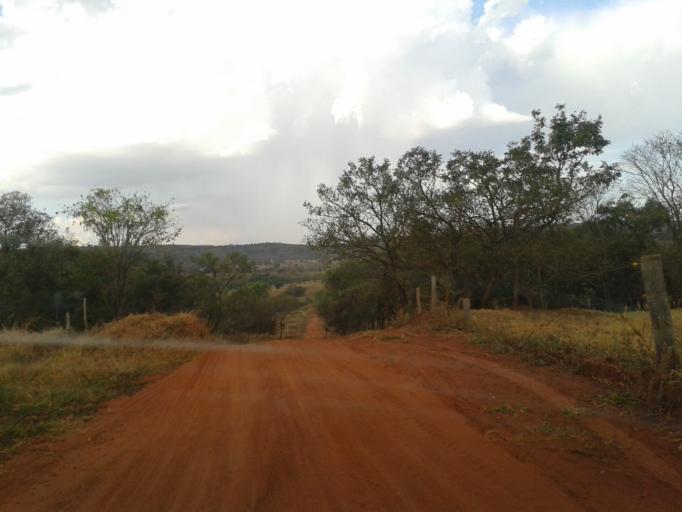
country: BR
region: Minas Gerais
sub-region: Santa Vitoria
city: Santa Vitoria
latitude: -19.1965
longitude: -49.9229
